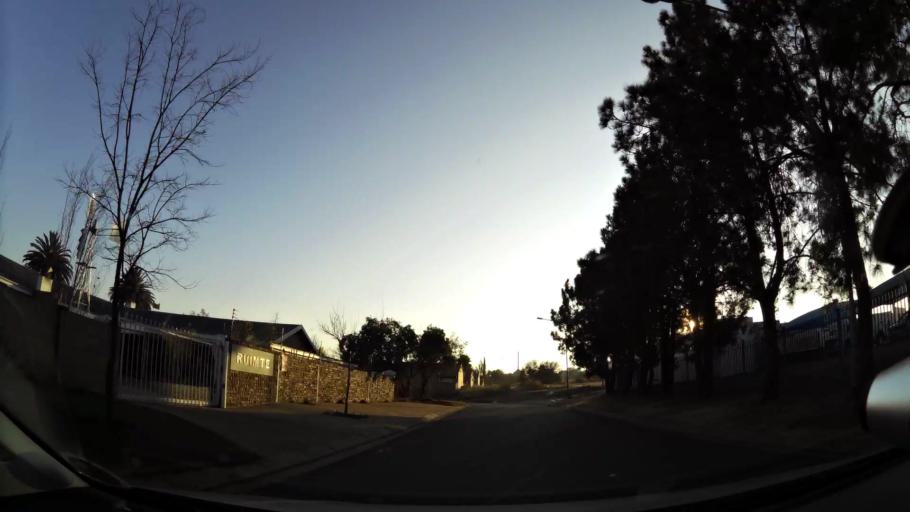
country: ZA
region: Orange Free State
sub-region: Mangaung Metropolitan Municipality
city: Bloemfontein
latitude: -29.0858
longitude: 26.1617
